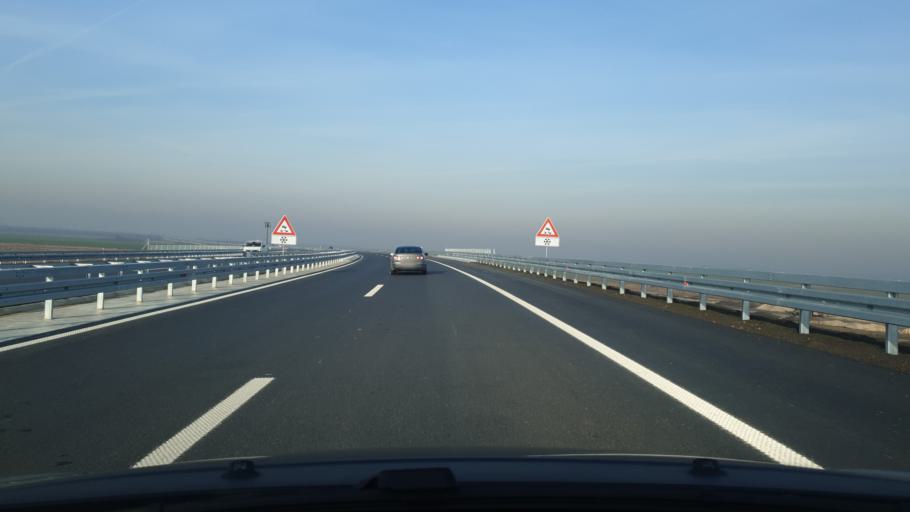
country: RS
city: Umka
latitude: 44.6888
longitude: 20.2675
